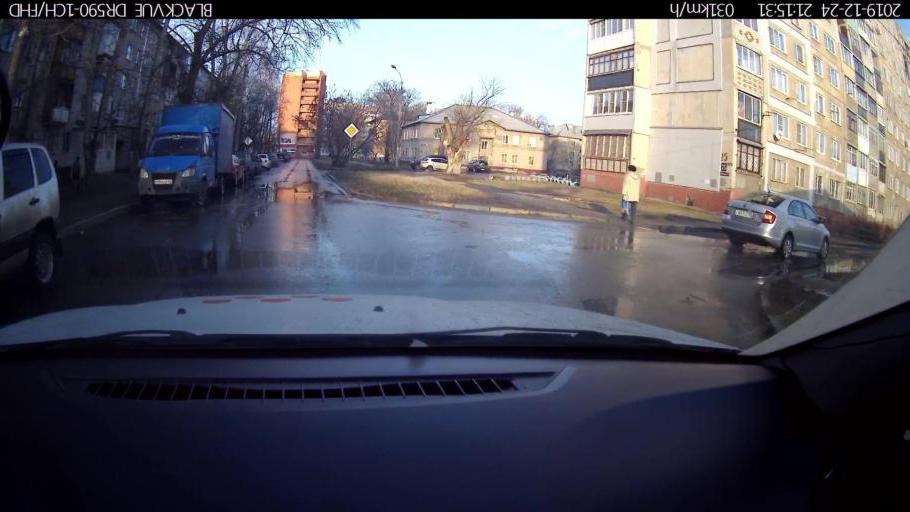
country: RU
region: Nizjnij Novgorod
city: Nizhniy Novgorod
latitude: 56.2661
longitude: 43.8840
